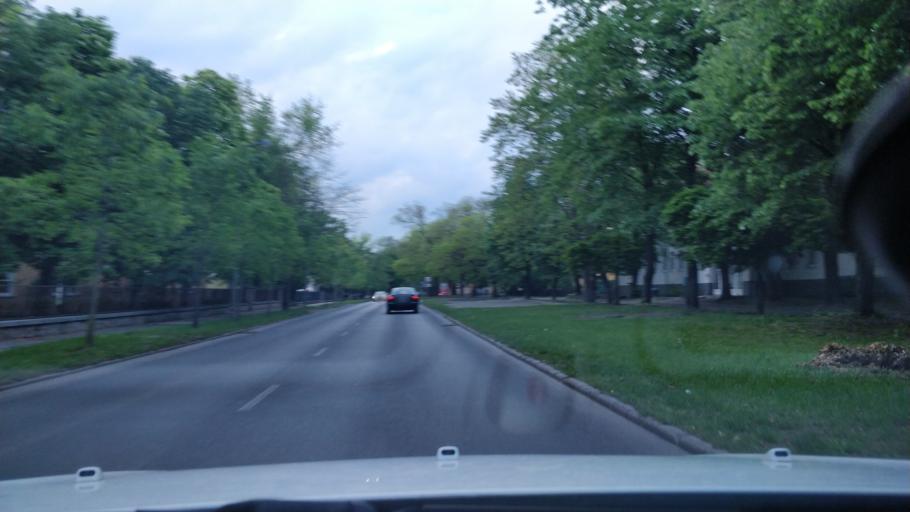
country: HU
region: Bacs-Kiskun
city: Kecskemet
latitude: 46.9097
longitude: 19.6775
